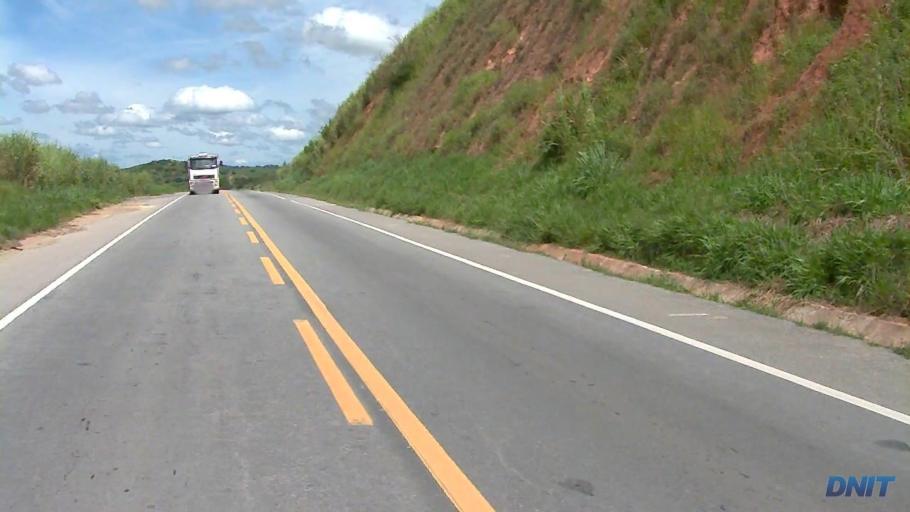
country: BR
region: Minas Gerais
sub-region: Governador Valadares
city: Governador Valadares
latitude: -18.9747
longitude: -42.0967
